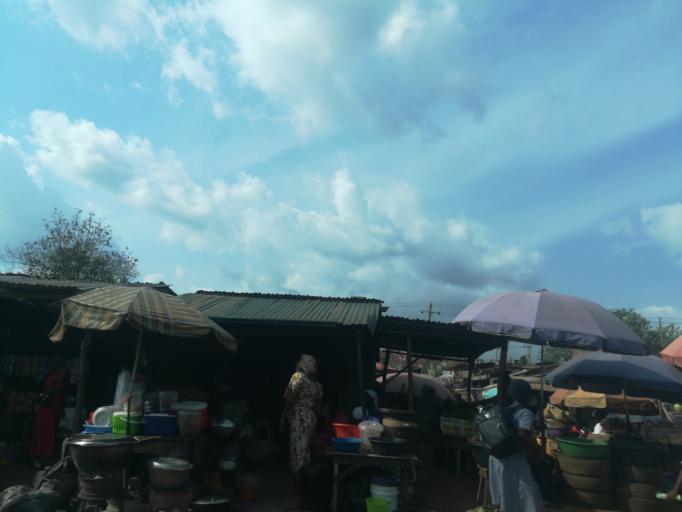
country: NG
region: Oyo
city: Ido
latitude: 7.3987
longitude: 3.8002
